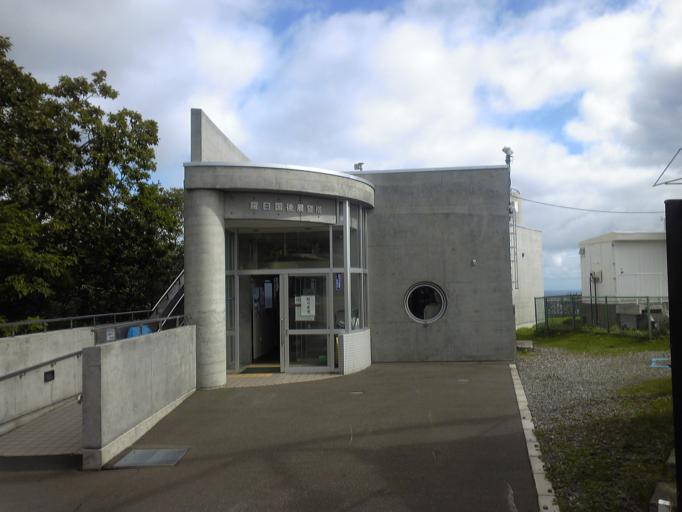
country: JP
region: Hokkaido
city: Shibetsu
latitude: 44.0153
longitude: 145.1860
